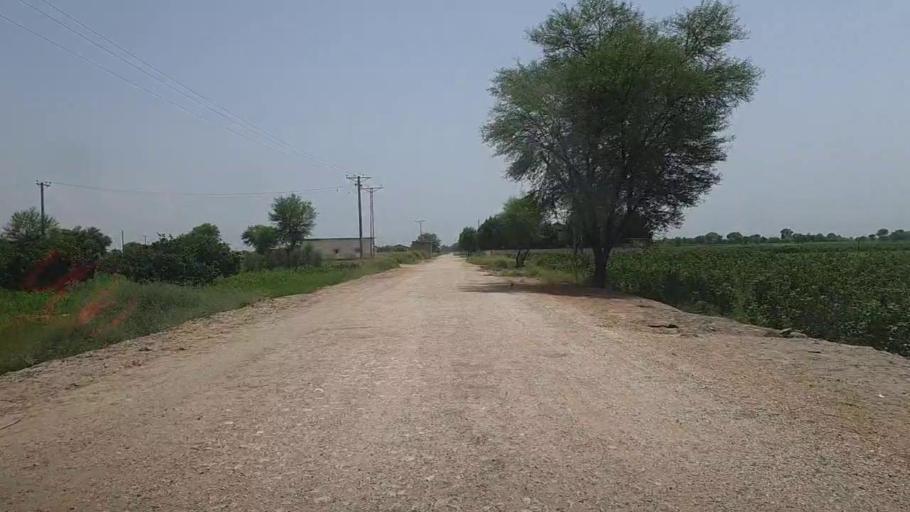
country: PK
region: Sindh
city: Pad Idan
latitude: 26.8407
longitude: 68.3247
